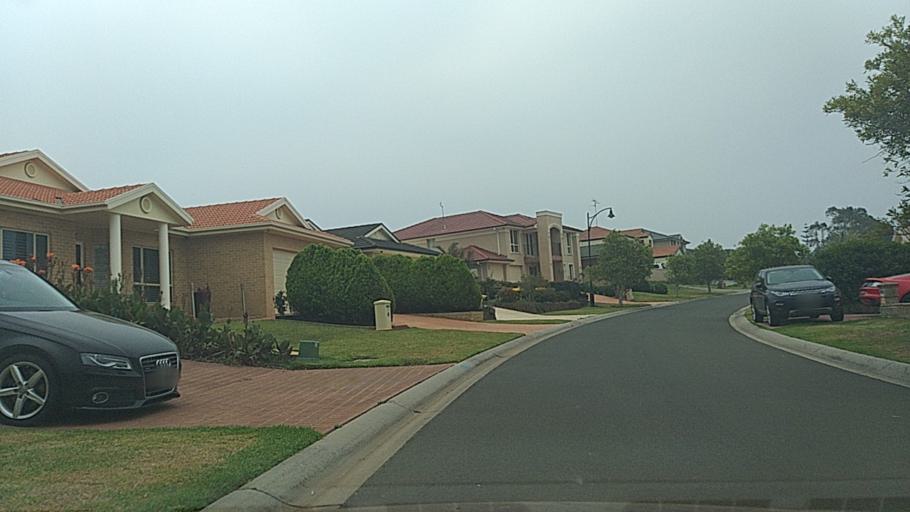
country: AU
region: New South Wales
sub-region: Shellharbour
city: Flinders
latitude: -34.5930
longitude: 150.8518
